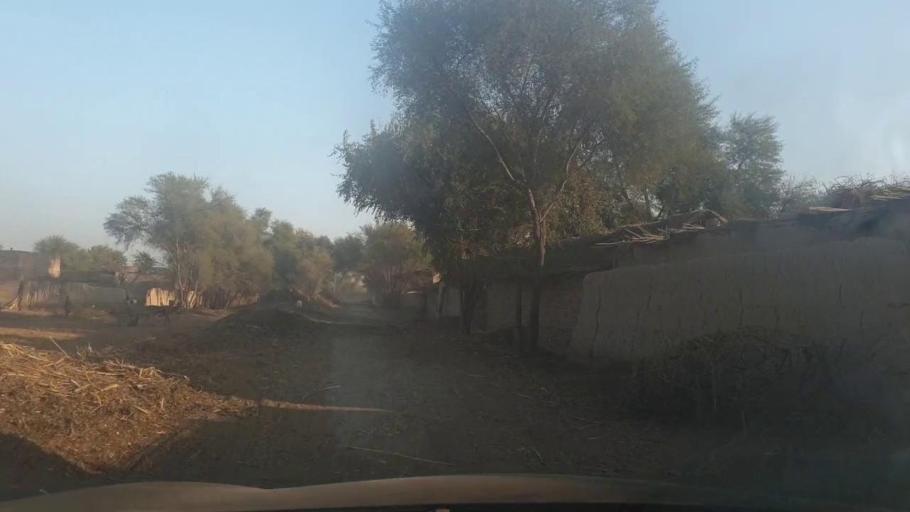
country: PK
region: Sindh
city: Mirpur Mathelo
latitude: 28.1726
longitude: 69.5759
